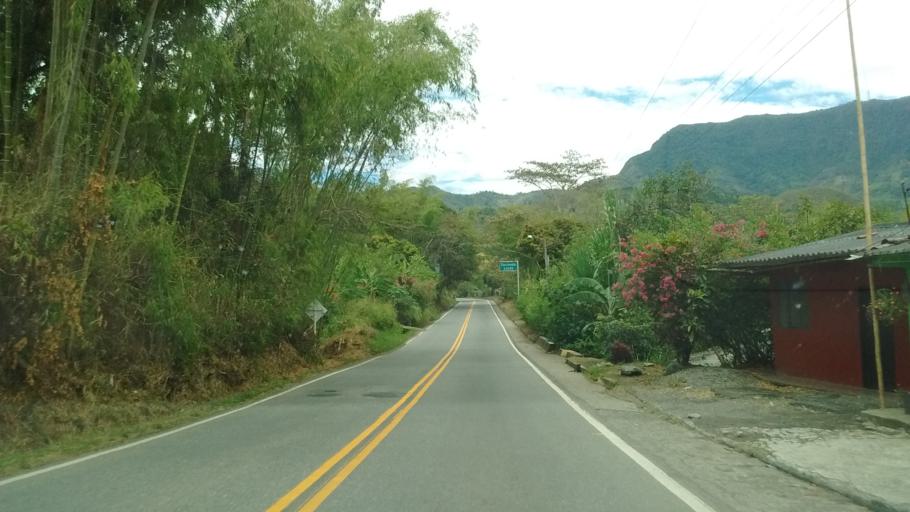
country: CO
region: Cauca
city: Rosas
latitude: 2.2319
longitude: -76.7866
